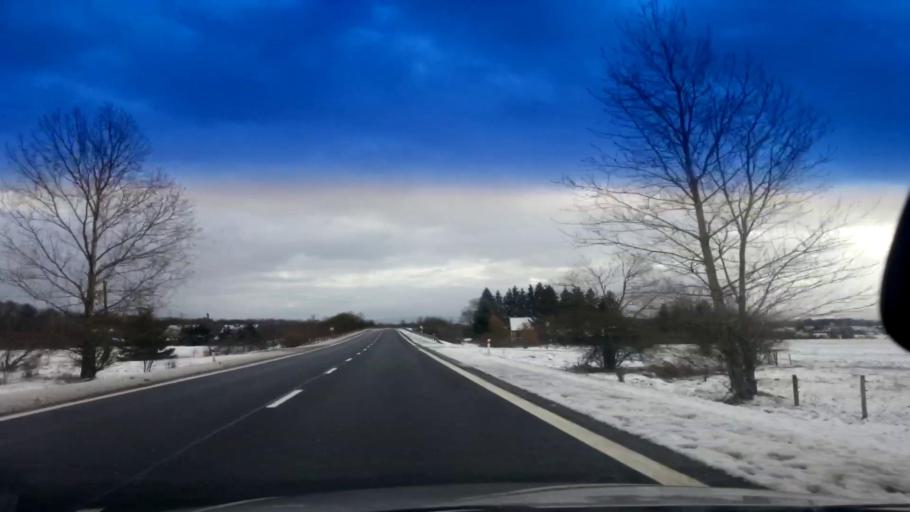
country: CZ
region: Karlovarsky
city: Hazlov
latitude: 50.1673
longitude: 12.2656
